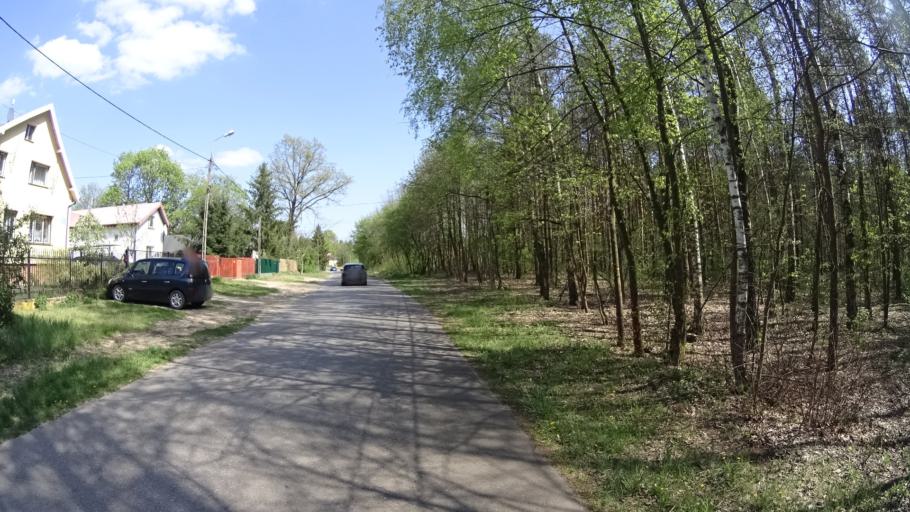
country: PL
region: Masovian Voivodeship
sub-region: Powiat warszawski zachodni
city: Izabelin
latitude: 52.3129
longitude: 20.8102
